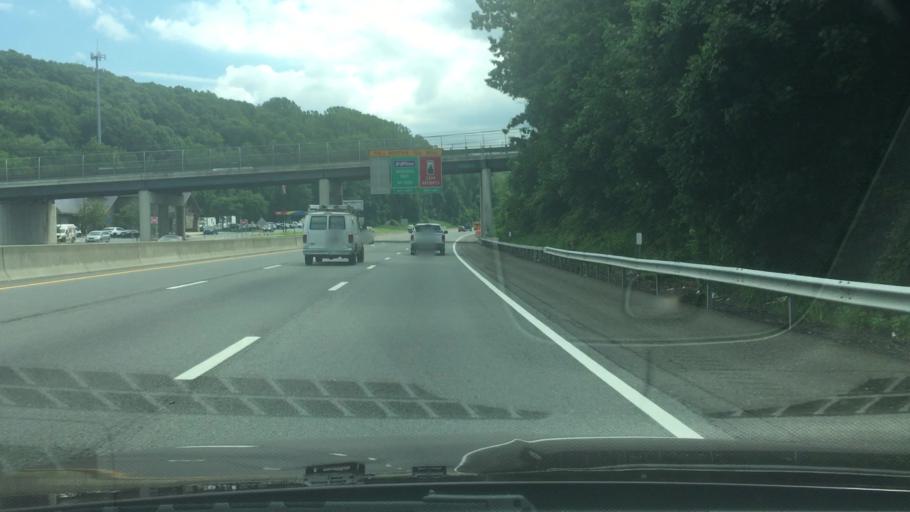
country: US
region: New York
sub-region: Westchester County
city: Ardsley
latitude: 40.9868
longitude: -73.8533
